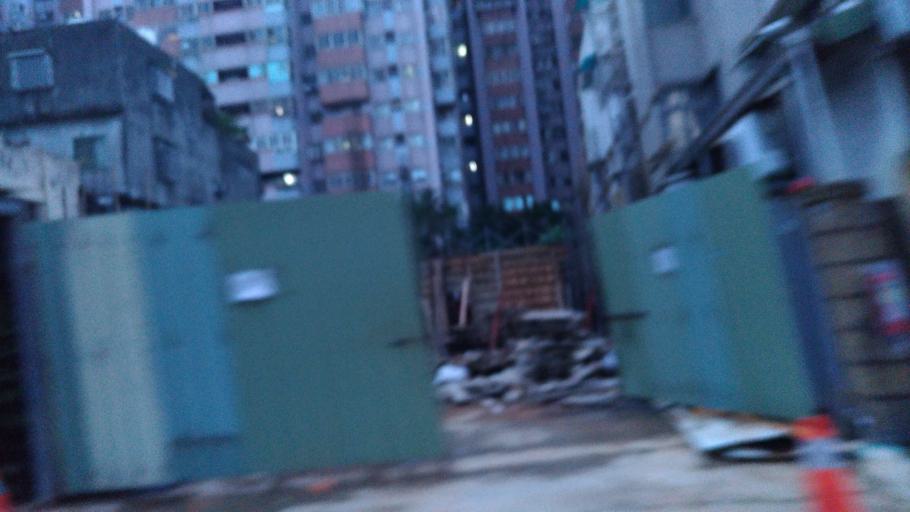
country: TW
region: Taiwan
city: Taoyuan City
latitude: 24.9570
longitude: 121.2973
